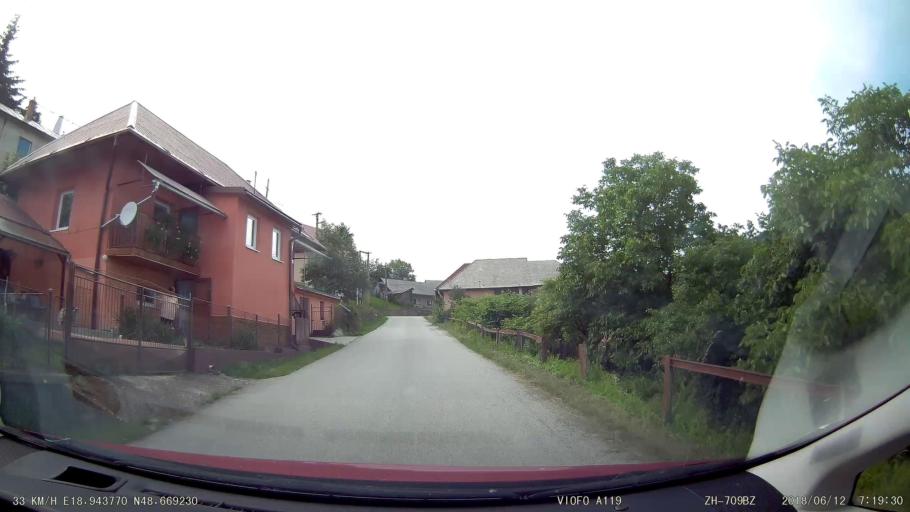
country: SK
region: Banskobystricky
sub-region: Okres Ziar nad Hronom
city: Kremnica
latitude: 48.6693
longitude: 18.9437
